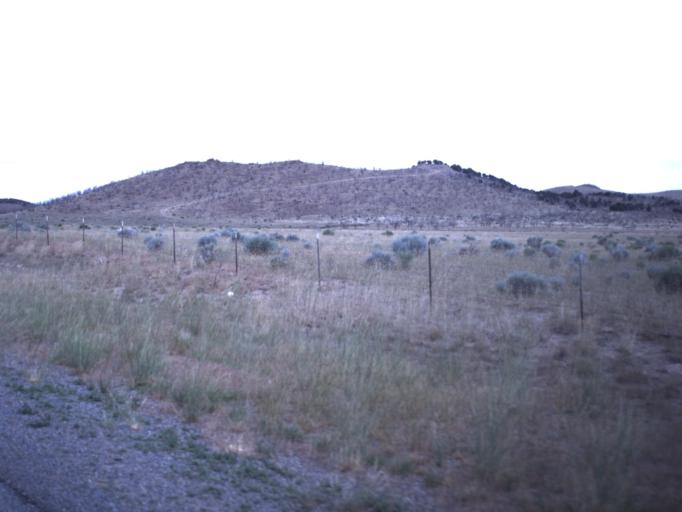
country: US
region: Utah
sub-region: Beaver County
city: Beaver
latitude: 38.6096
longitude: -112.5972
